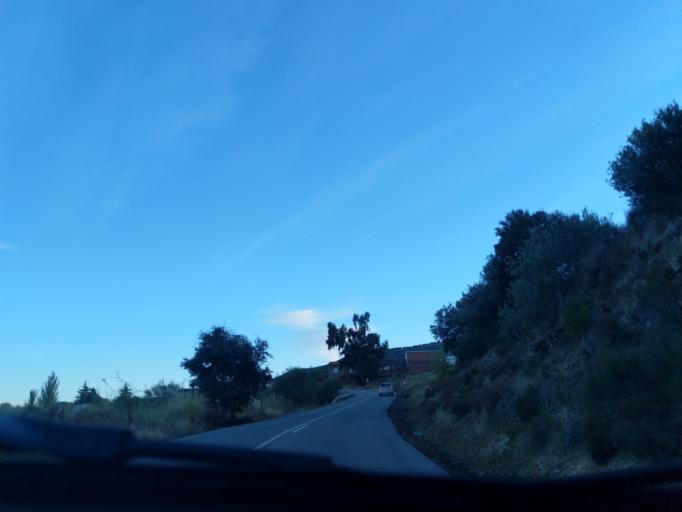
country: ES
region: Extremadura
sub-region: Provincia de Badajoz
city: Reina
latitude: 38.1571
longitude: -5.8975
